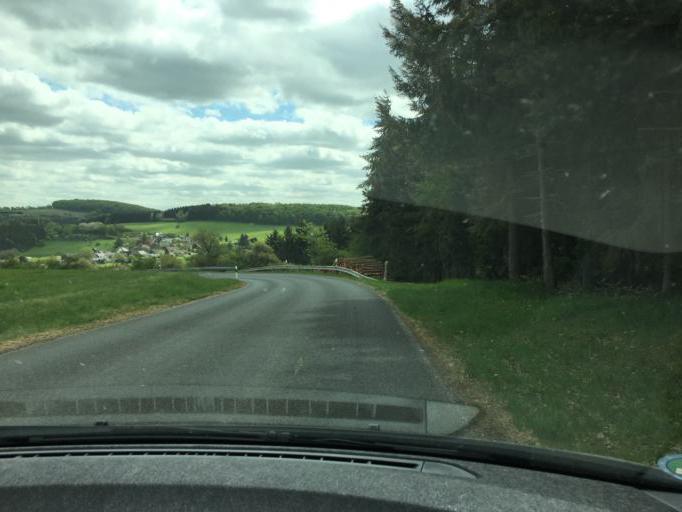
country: DE
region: Rheinland-Pfalz
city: Kirchsahr
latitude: 50.5025
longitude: 6.9023
